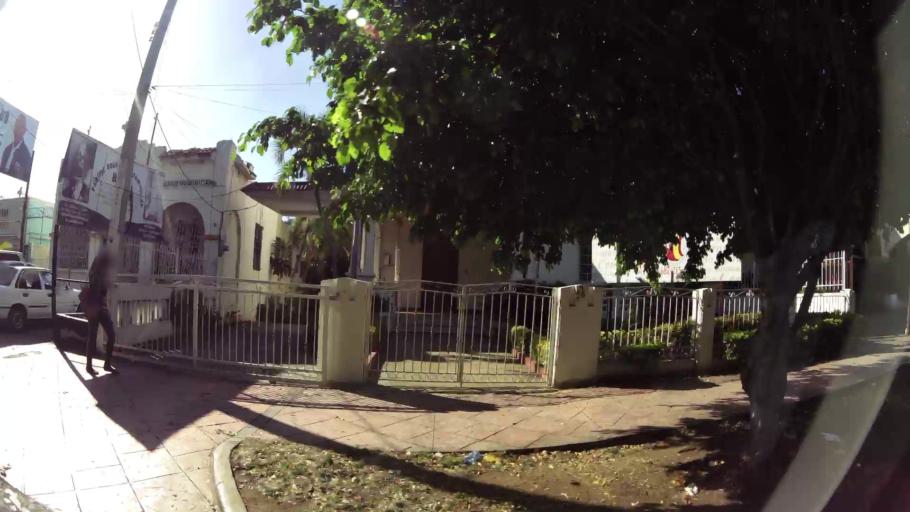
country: DO
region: Nacional
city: Ciudad Nueva
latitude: 18.4709
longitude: -69.8957
